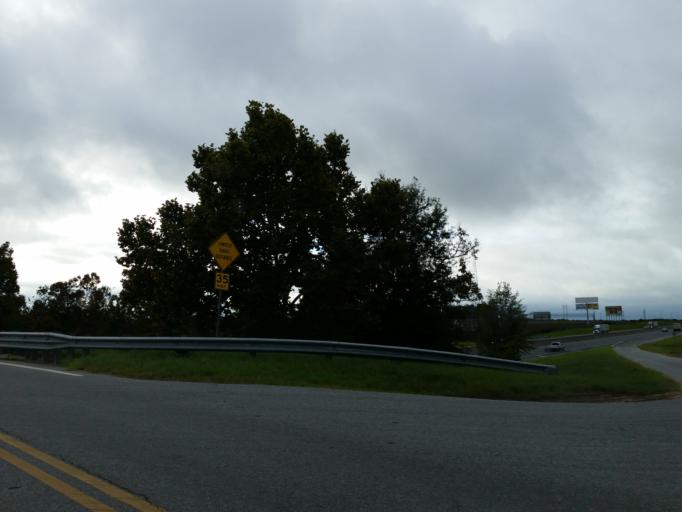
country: US
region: Georgia
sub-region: Tift County
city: Tifton
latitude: 31.5702
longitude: -83.5467
